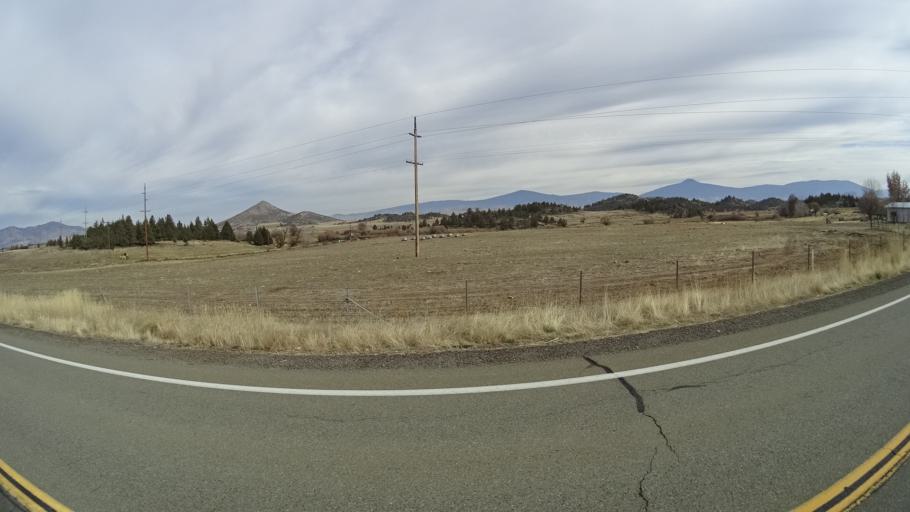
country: US
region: California
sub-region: Siskiyou County
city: Montague
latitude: 41.6844
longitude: -122.5341
